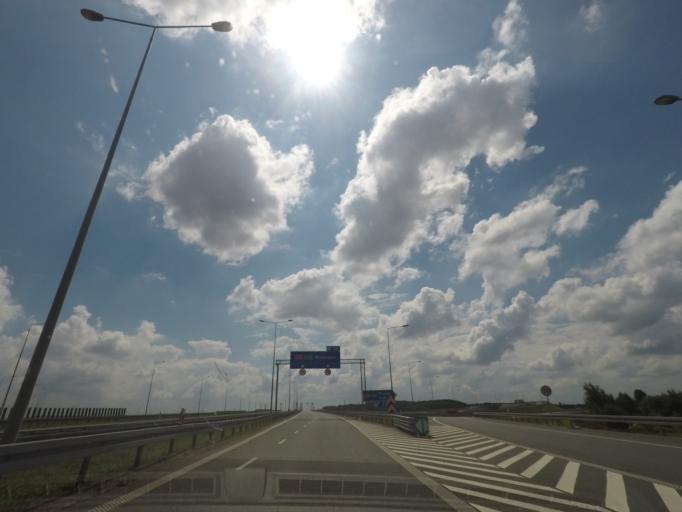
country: PL
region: Lodz Voivodeship
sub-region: Powiat zgierski
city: Strykow
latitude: 51.8950
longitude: 19.6318
